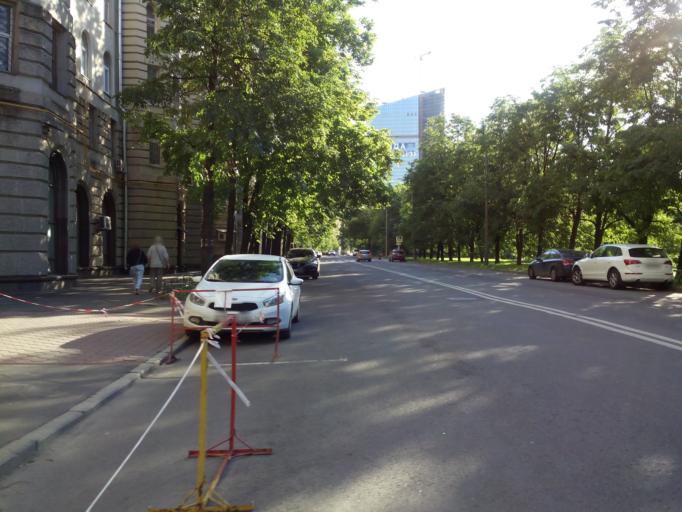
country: RU
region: Moskovskaya
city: Presnenskiy
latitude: 55.7443
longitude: 37.5420
